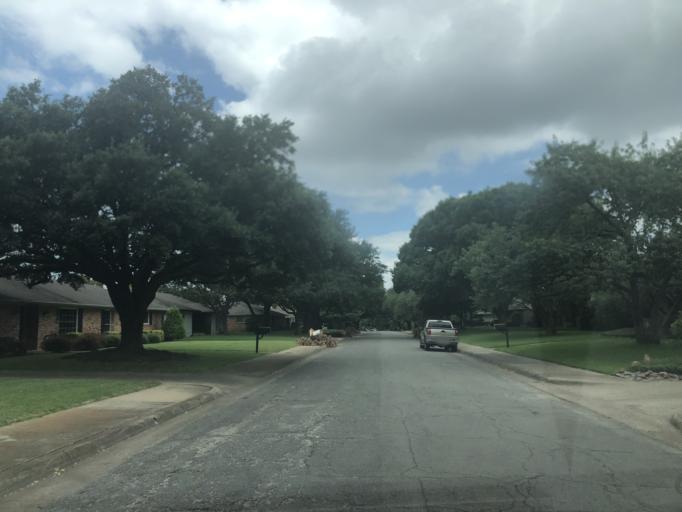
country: US
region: Texas
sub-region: Dallas County
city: University Park
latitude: 32.8895
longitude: -96.8337
